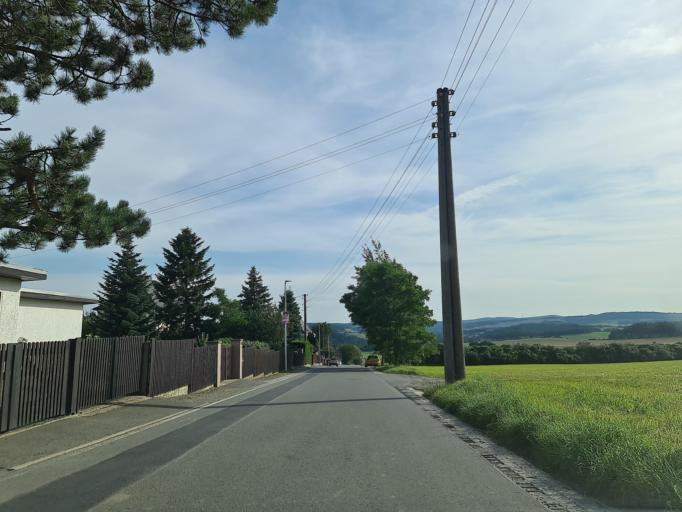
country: DE
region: Saxony
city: Weischlitz
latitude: 50.4892
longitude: 12.0900
